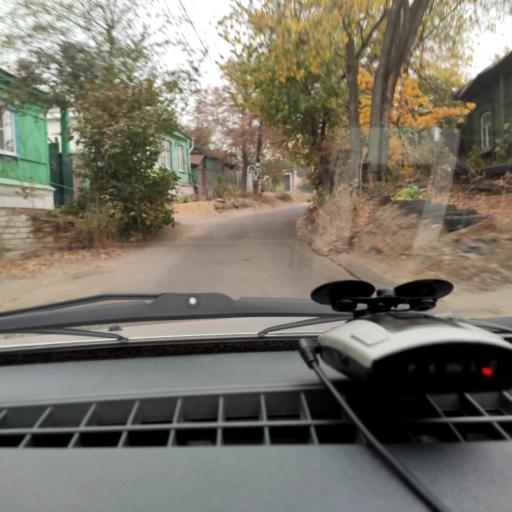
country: RU
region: Voronezj
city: Voronezh
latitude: 51.6864
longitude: 39.2244
